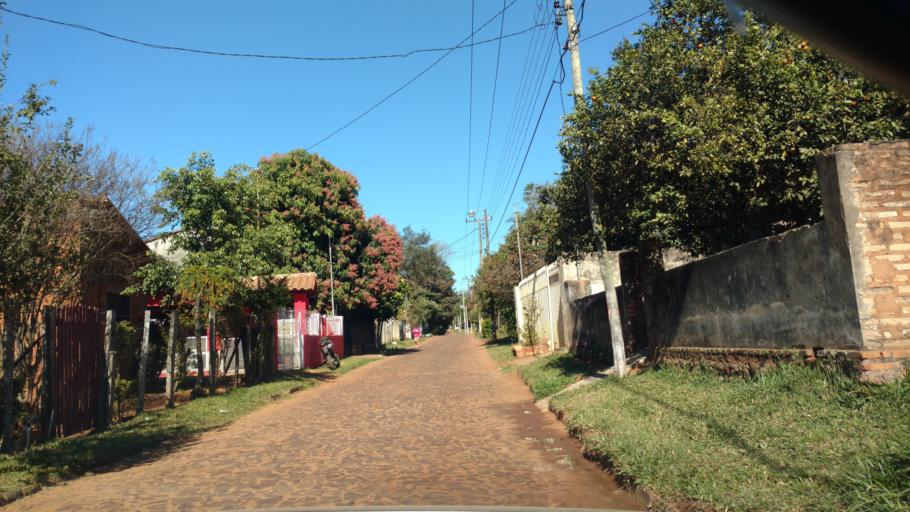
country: PY
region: Central
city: Capiata
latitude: -25.3575
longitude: -57.4153
